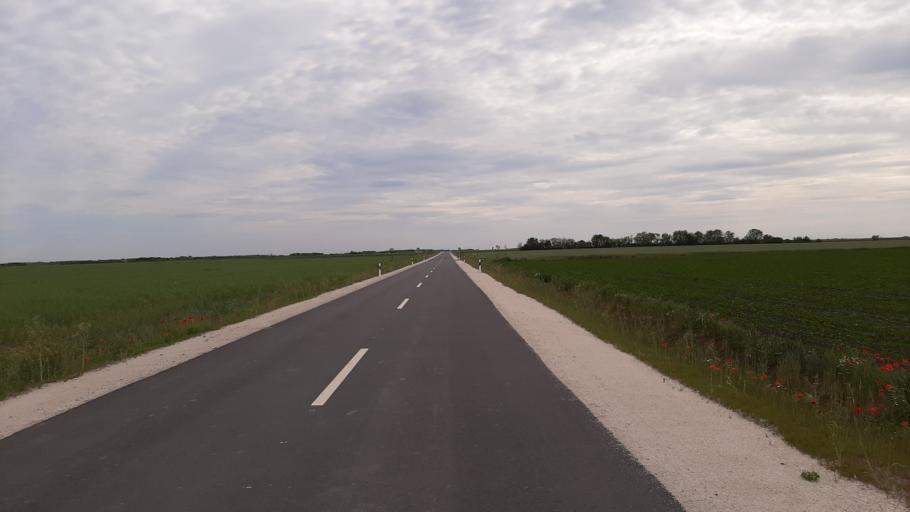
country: RO
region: Timis
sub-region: Comuna Beba Veche
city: Beba Veche
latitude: 46.1403
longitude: 20.2755
